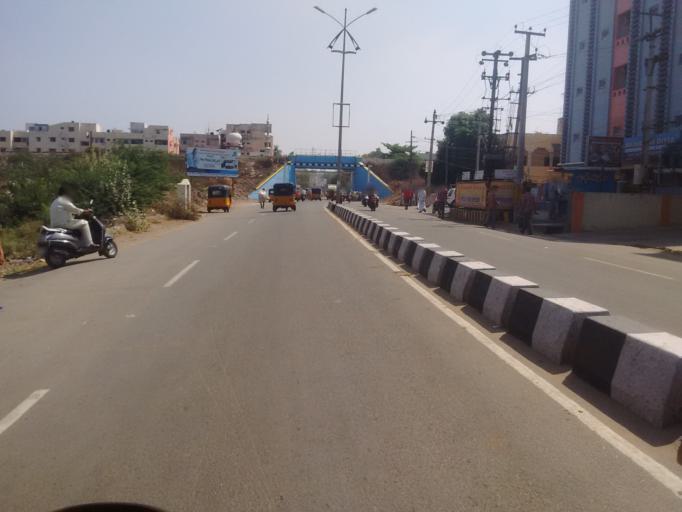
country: IN
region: Telangana
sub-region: Mahbubnagar
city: Alampur
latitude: 15.8414
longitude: 78.0345
